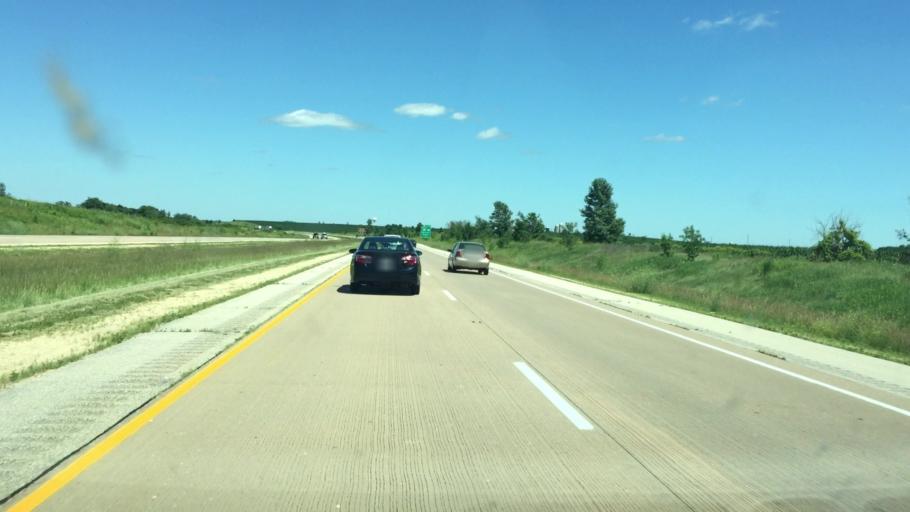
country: US
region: Wisconsin
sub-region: Grant County
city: Platteville
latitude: 42.7391
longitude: -90.3668
